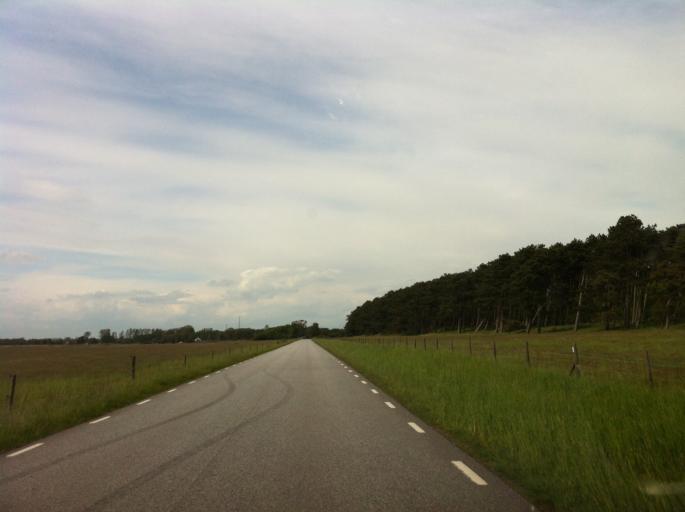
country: SE
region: Skane
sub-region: Kavlinge Kommun
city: Hofterup
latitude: 55.8071
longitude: 12.9371
